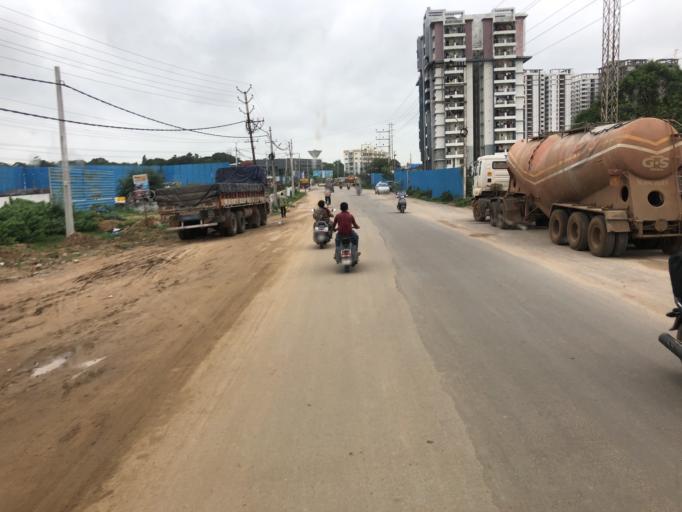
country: IN
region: Telangana
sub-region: Medak
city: Serilingampalle
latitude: 17.4665
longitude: 78.3376
